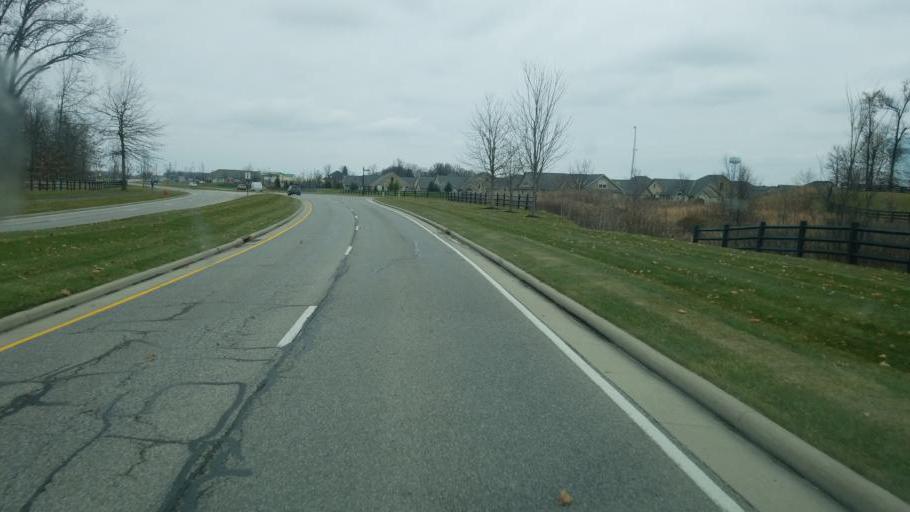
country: US
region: Ohio
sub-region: Delaware County
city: Powell
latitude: 40.1899
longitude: -83.0959
